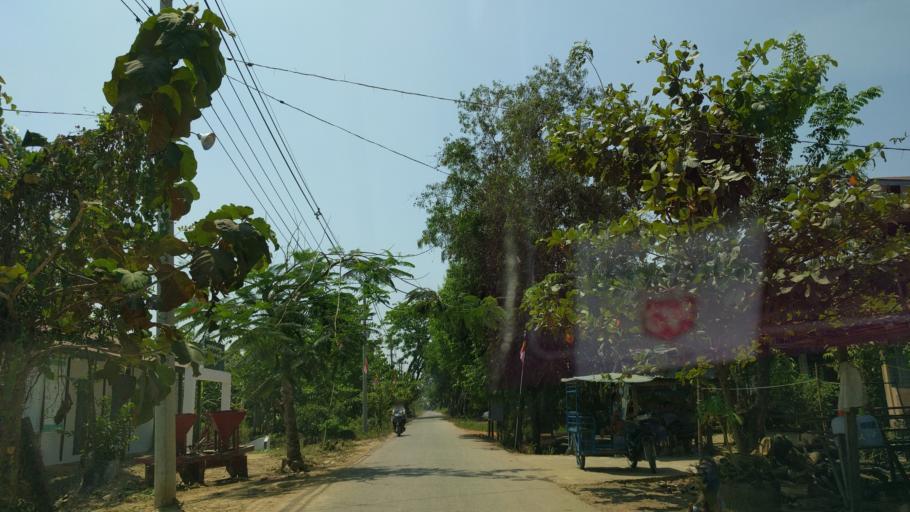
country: MM
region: Mon
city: Martaban
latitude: 16.6092
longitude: 97.6646
